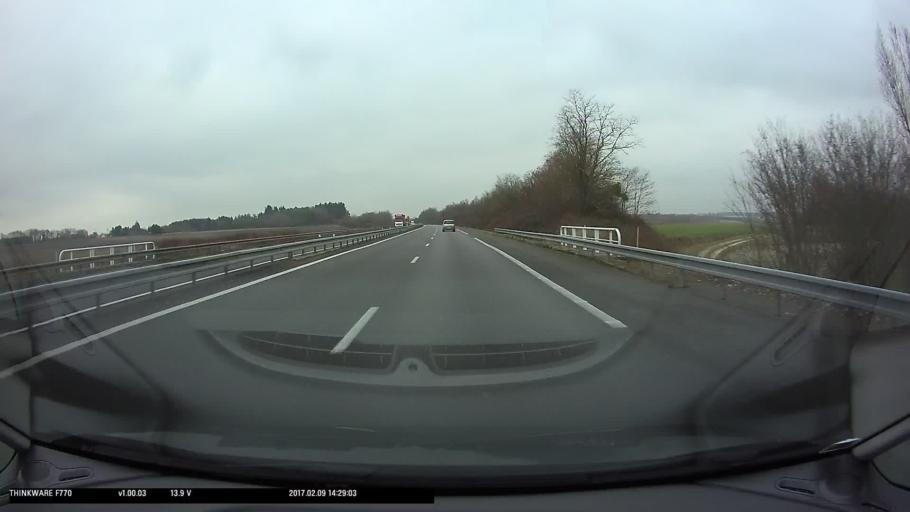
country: FR
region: Centre
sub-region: Departement du Cher
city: Mehun-sur-Yevre
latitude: 47.1199
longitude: 2.1943
